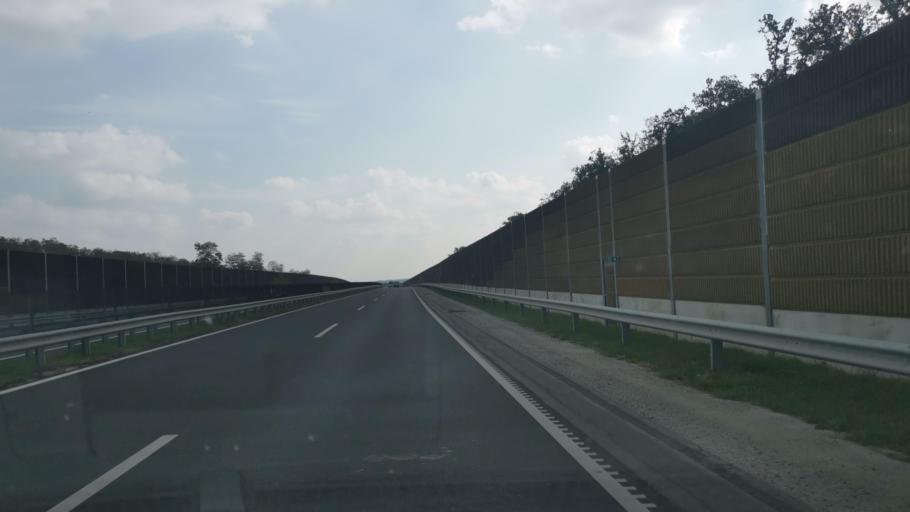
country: AT
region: Burgenland
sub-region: Politischer Bezirk Oberpullendorf
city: Deutschkreutz
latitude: 47.6239
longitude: 16.6535
